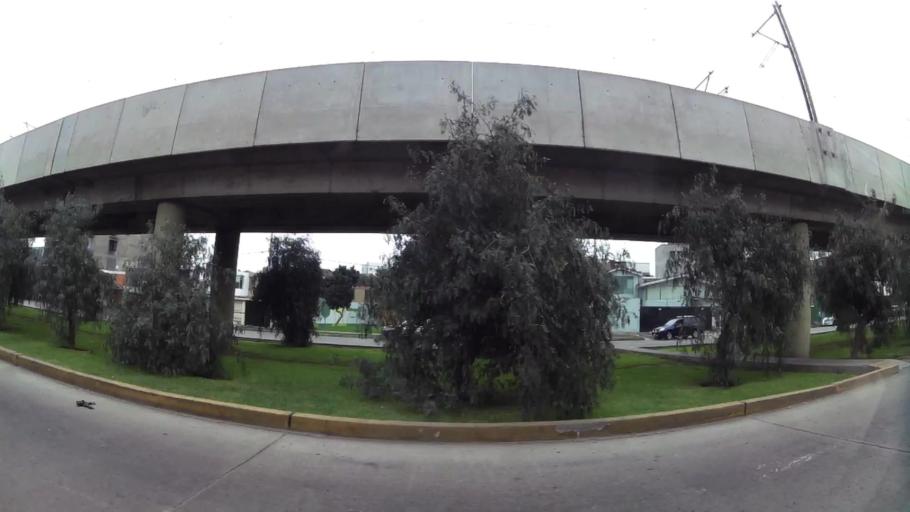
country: PE
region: Lima
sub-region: Lima
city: Surco
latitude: -12.1214
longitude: -76.9982
